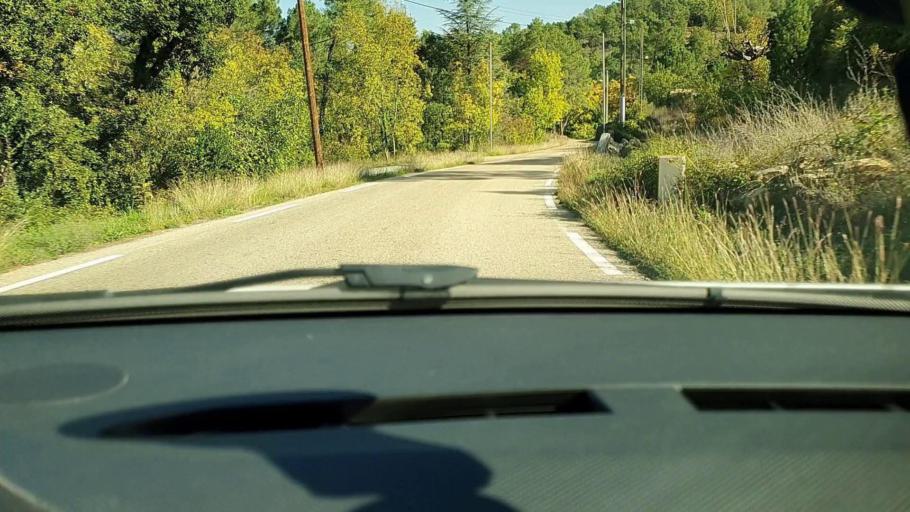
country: FR
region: Languedoc-Roussillon
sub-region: Departement du Gard
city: Molieres-sur-Ceze
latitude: 44.2530
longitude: 4.1355
